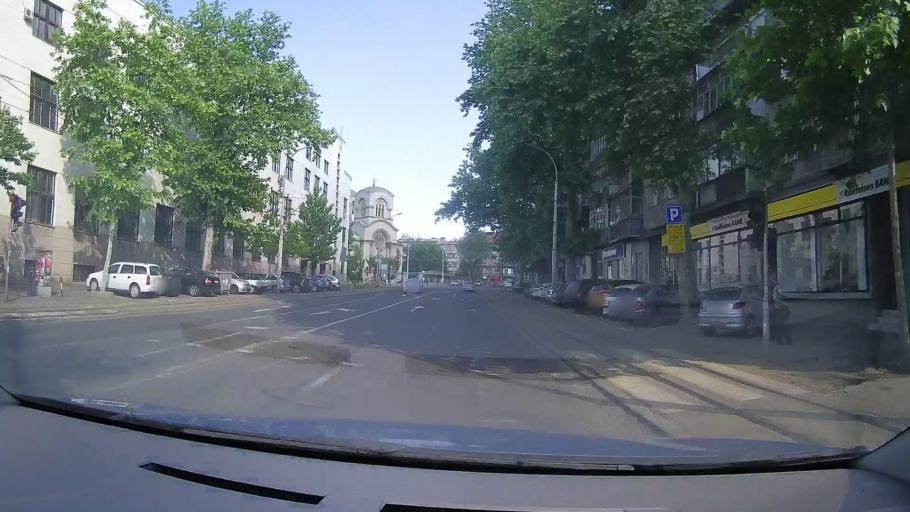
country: RS
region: Central Serbia
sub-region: Belgrade
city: Stari Grad
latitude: 44.8209
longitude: 20.4647
